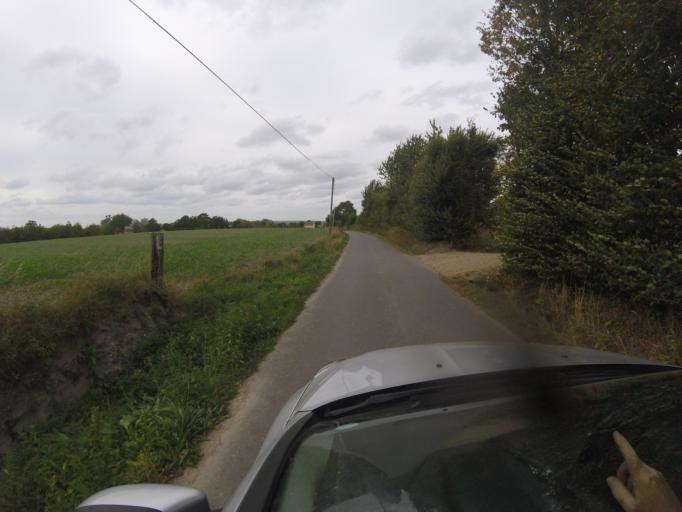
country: FR
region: Lower Normandy
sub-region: Departement de la Manche
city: Le Val-Saint-Pere
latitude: 48.6338
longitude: -1.3881
